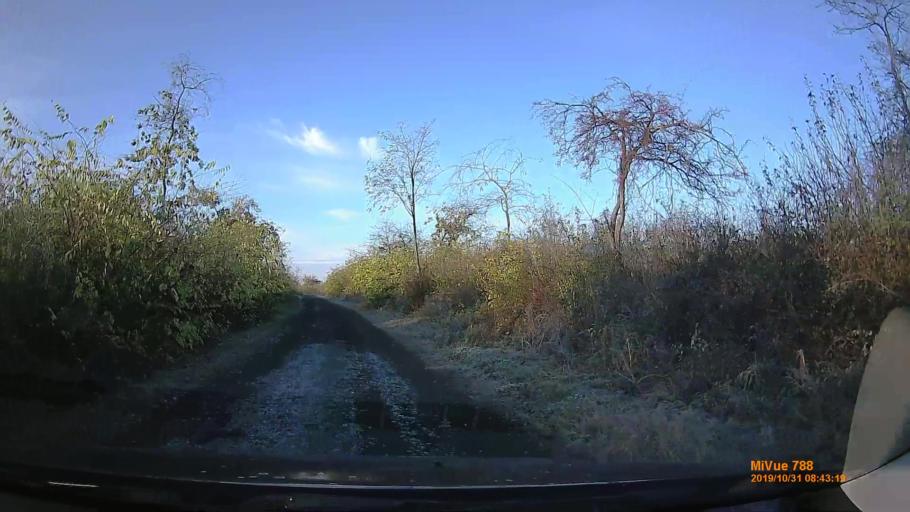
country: HU
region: Pest
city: Pand
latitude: 47.2996
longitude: 19.6282
